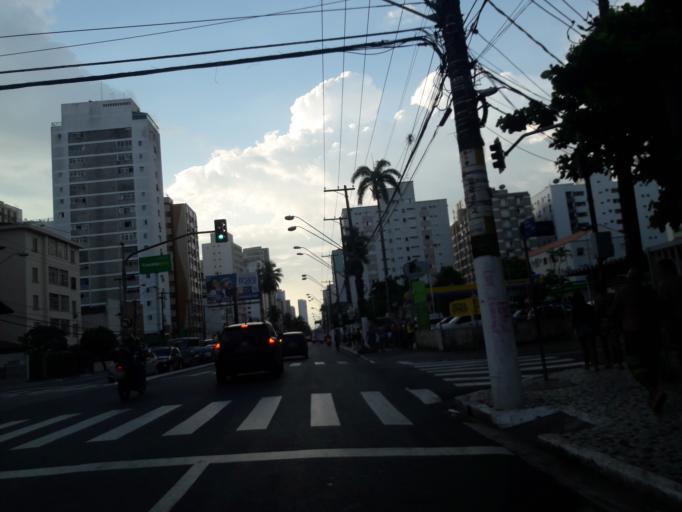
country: BR
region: Sao Paulo
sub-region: Sao Vicente
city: Sao Vicente
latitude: -23.9715
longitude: -46.3705
